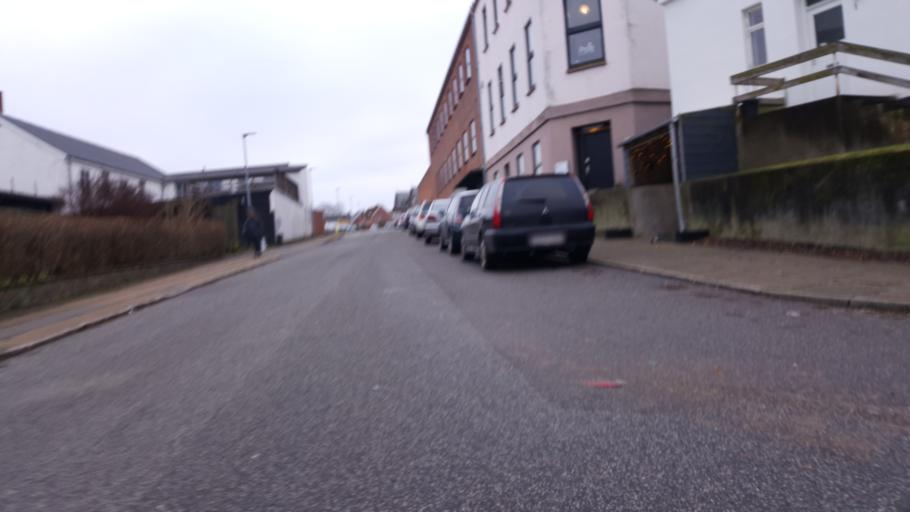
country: DK
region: South Denmark
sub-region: Kolding Kommune
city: Kolding
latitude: 55.4842
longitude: 9.4756
